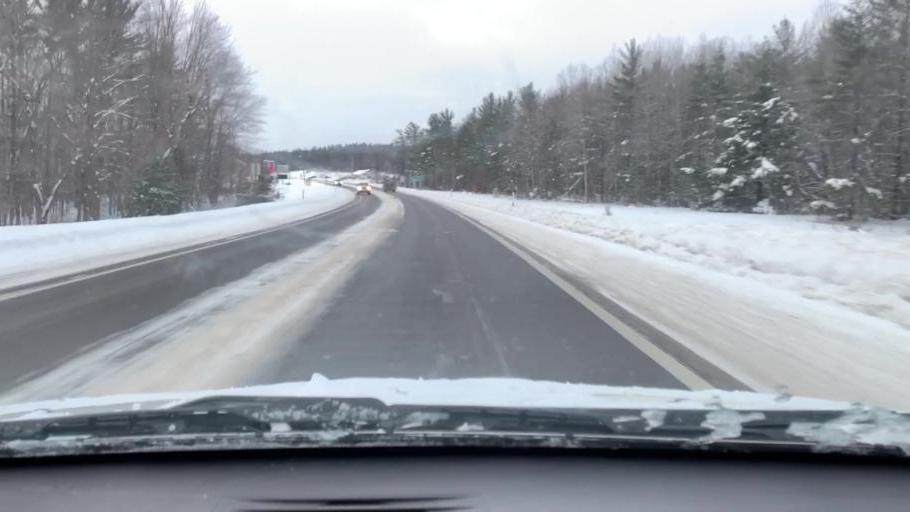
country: US
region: Michigan
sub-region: Kalkaska County
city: Kalkaska
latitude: 44.6434
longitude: -85.2840
